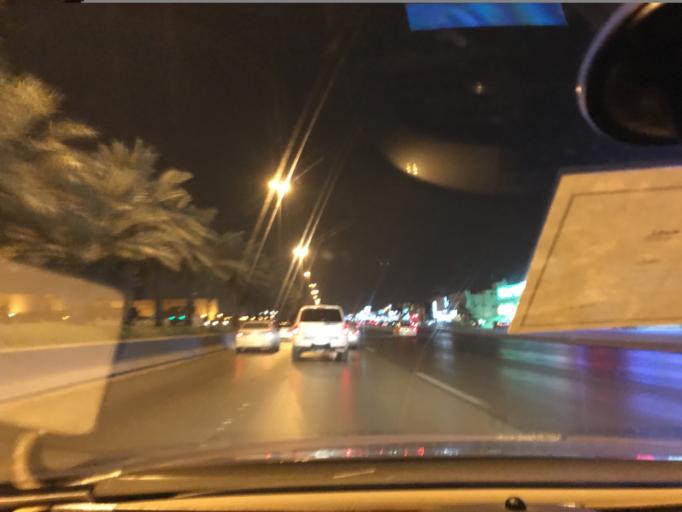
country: SA
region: Ar Riyad
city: Riyadh
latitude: 24.7438
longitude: 46.7471
